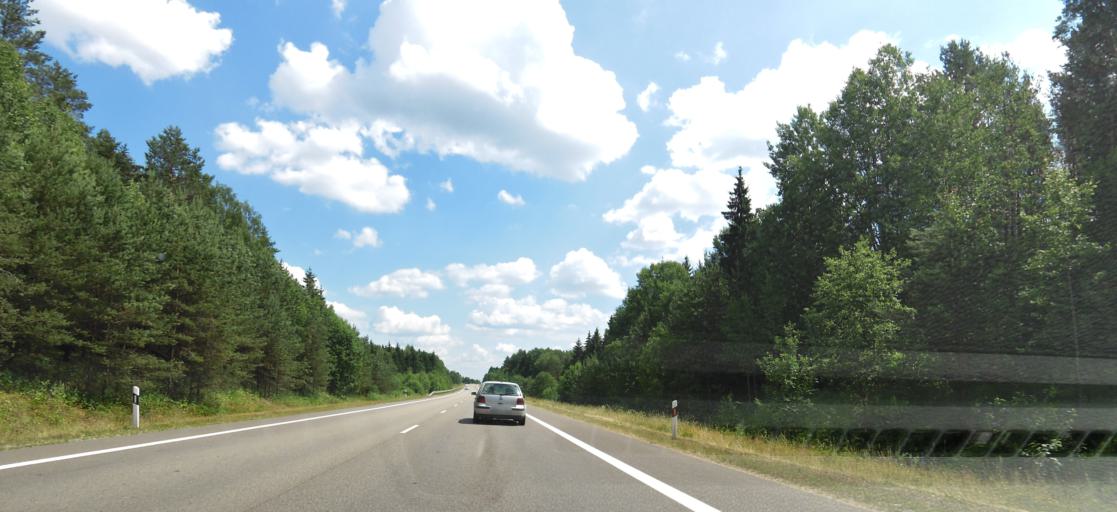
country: LT
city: Skaidiskes
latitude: 54.6135
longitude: 25.4337
